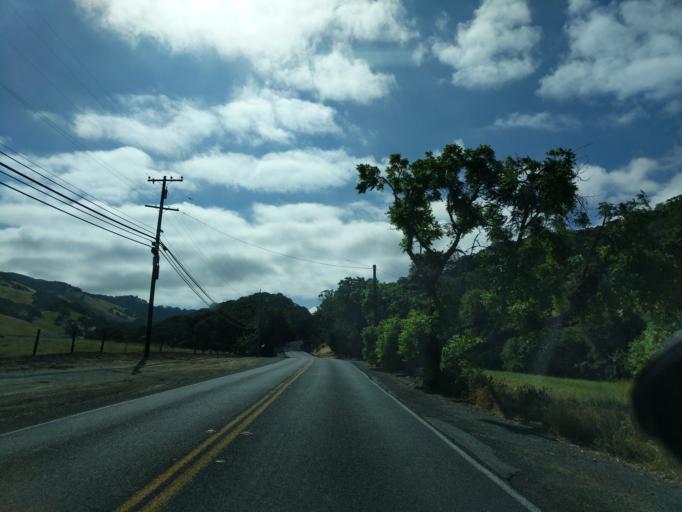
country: US
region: California
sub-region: Contra Costa County
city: Clayton
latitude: 37.9207
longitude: -121.9004
